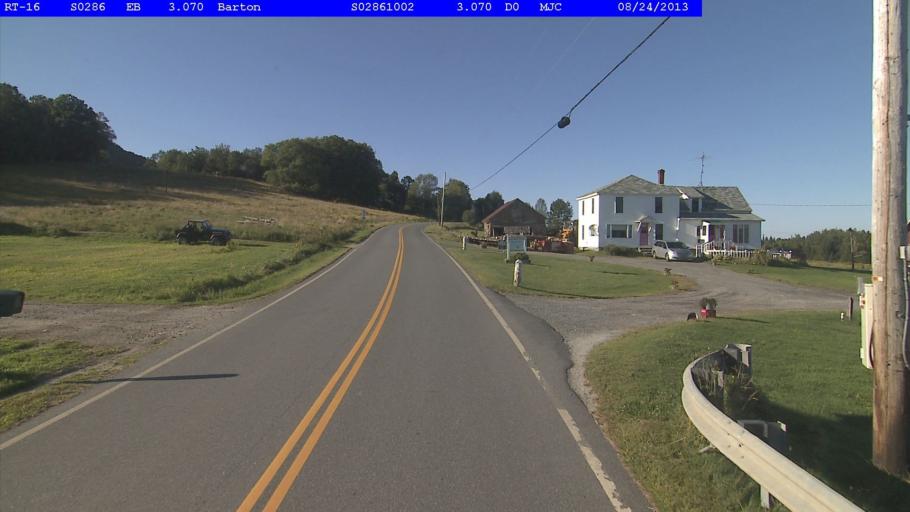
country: US
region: Vermont
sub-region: Orleans County
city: Newport
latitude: 44.7667
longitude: -72.1275
